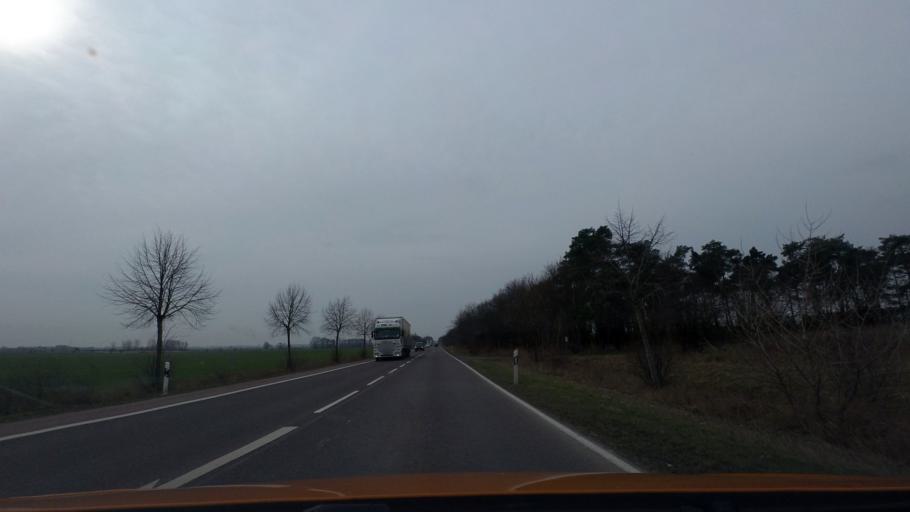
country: DE
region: Saxony-Anhalt
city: Moser
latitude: 52.1962
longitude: 11.7725
